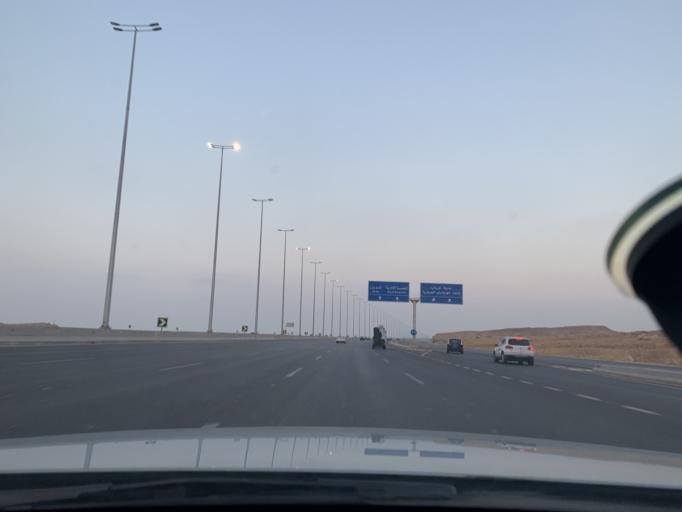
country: EG
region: Muhafazat al Qalyubiyah
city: Al Khankah
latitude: 30.0945
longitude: 31.4872
